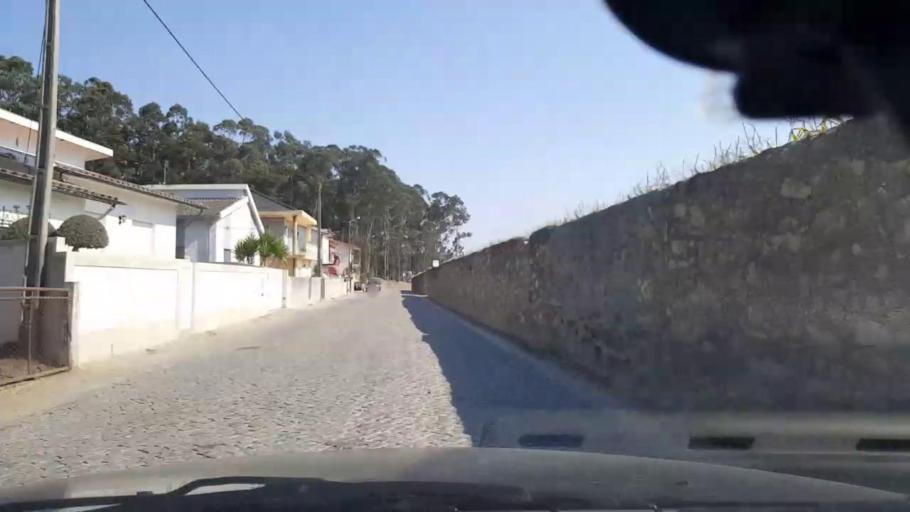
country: PT
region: Porto
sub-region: Povoa de Varzim
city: Pedroso
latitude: 41.4046
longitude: -8.6893
